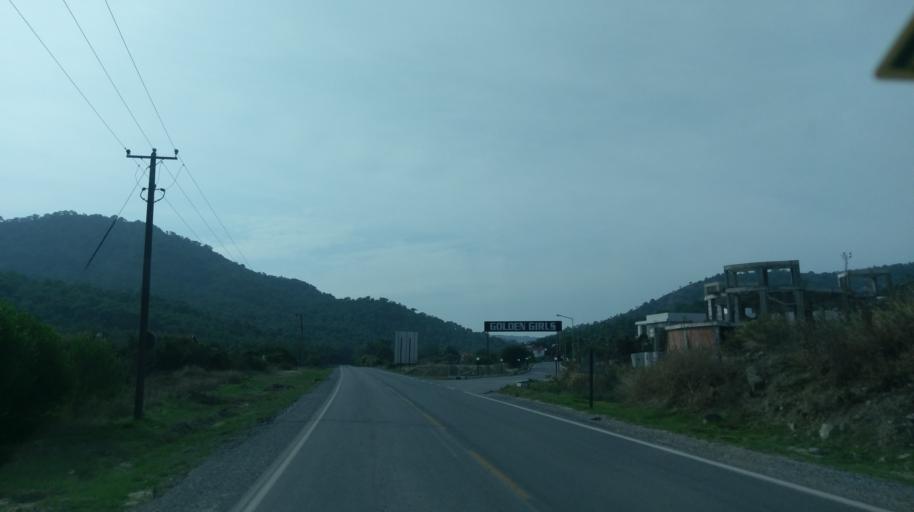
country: CY
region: Keryneia
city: Lapithos
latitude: 35.3485
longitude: 33.0827
